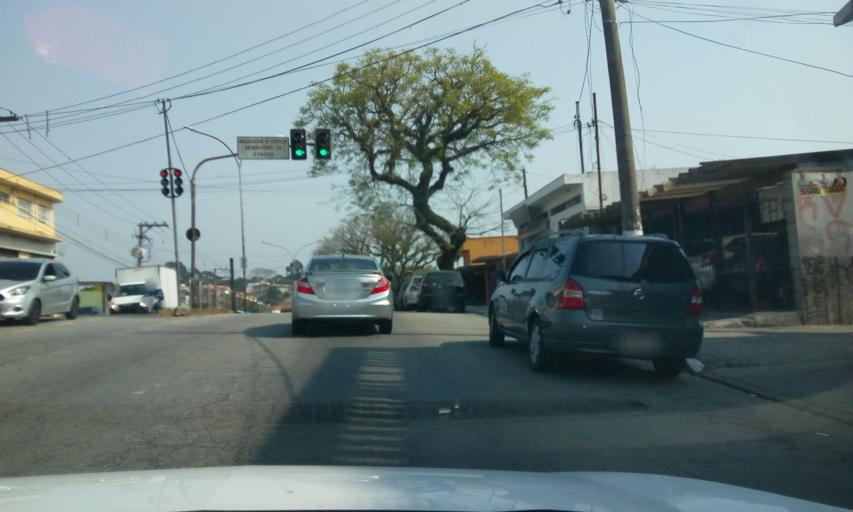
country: BR
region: Sao Paulo
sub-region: Diadema
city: Diadema
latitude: -23.7130
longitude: -46.6894
